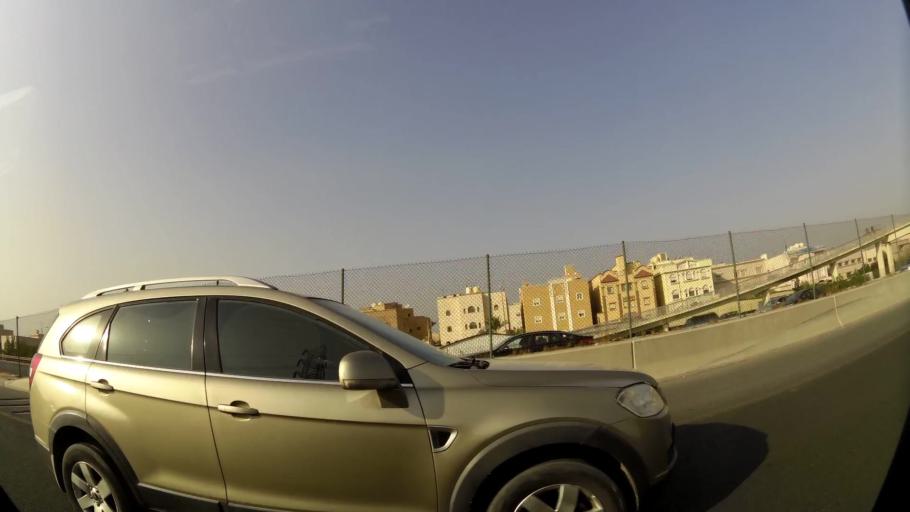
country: KW
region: Al Asimah
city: Ar Rabiyah
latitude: 29.2969
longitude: 47.8846
